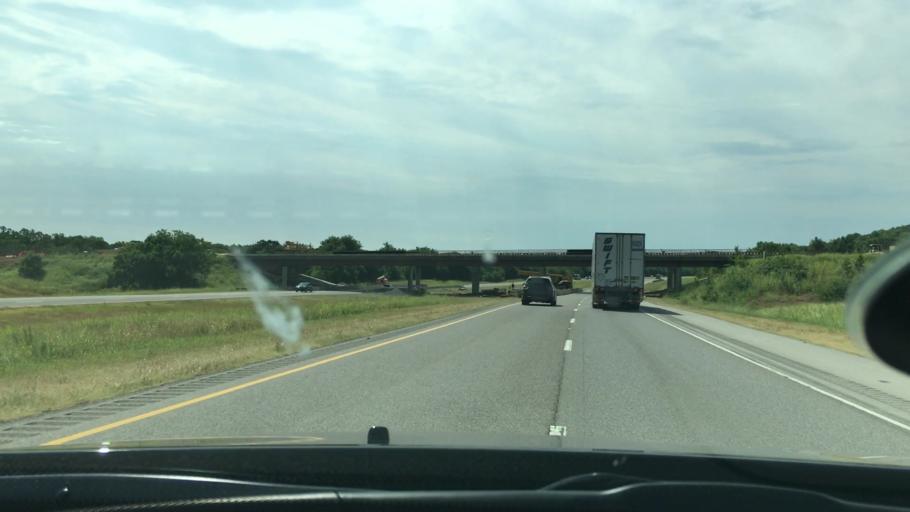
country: US
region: Oklahoma
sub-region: Murray County
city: Davis
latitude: 34.4895
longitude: -97.1626
